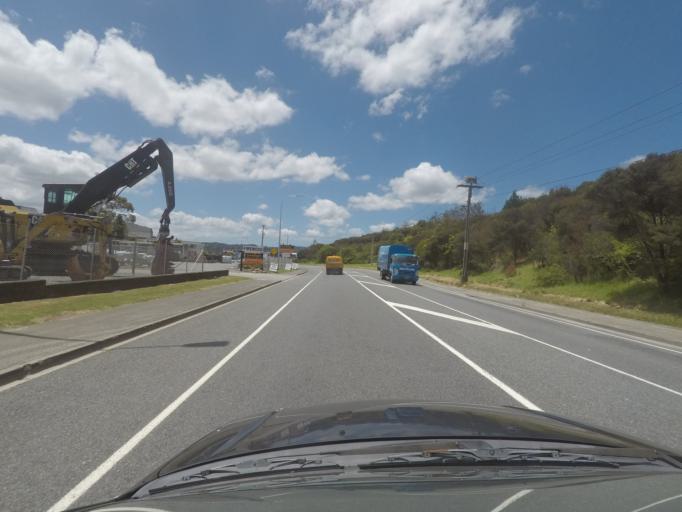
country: NZ
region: Northland
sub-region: Whangarei
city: Whangarei
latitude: -35.7428
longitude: 174.3299
